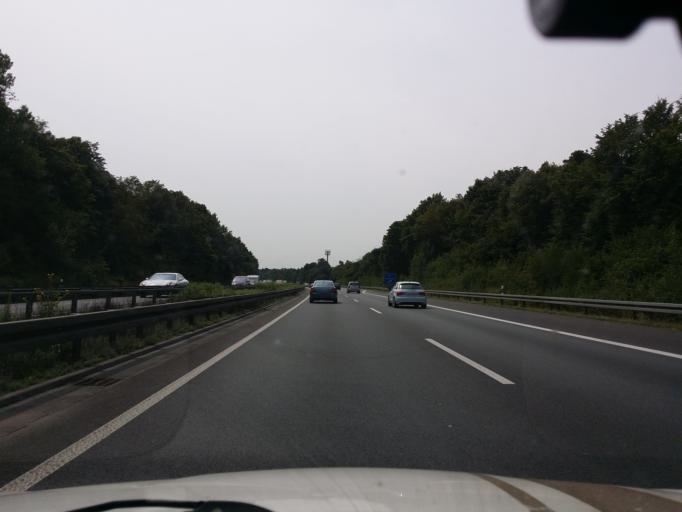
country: DE
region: Hesse
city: Pfungstadt
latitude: 49.7951
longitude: 8.6201
